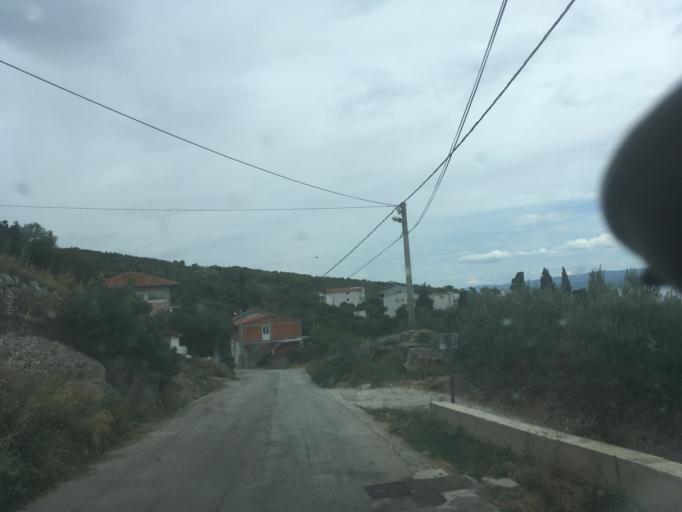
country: HR
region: Splitsko-Dalmatinska
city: Jesenice
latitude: 43.4556
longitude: 16.6224
